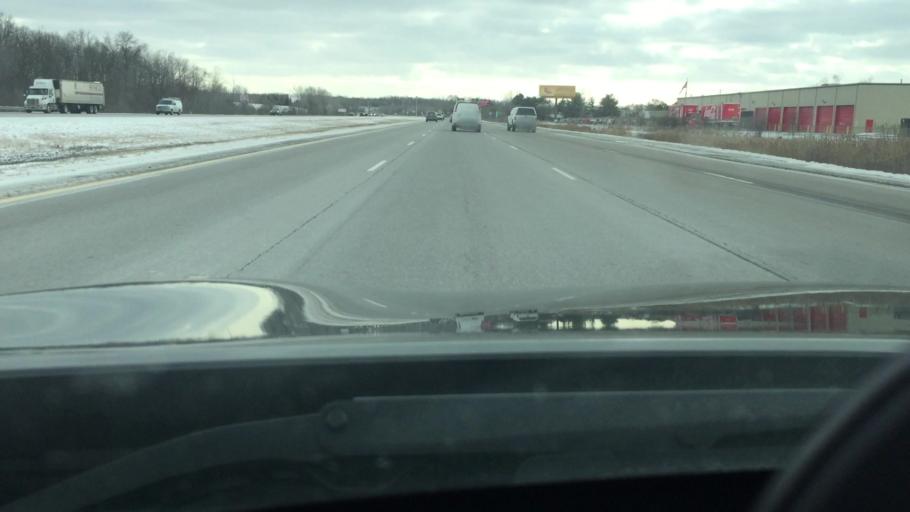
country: US
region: Michigan
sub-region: Wayne County
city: Romulus
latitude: 42.2442
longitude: -83.4401
